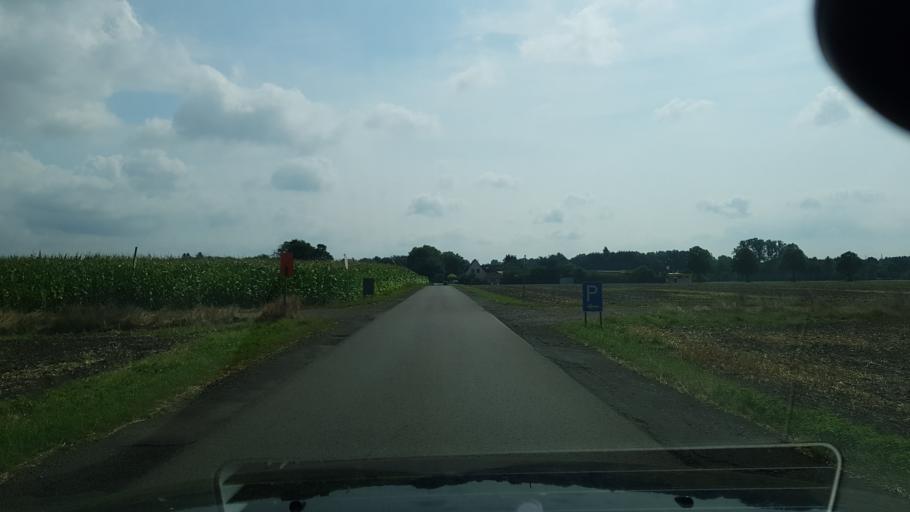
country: DE
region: Lower Saxony
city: Sulingen
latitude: 52.6781
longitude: 8.7853
